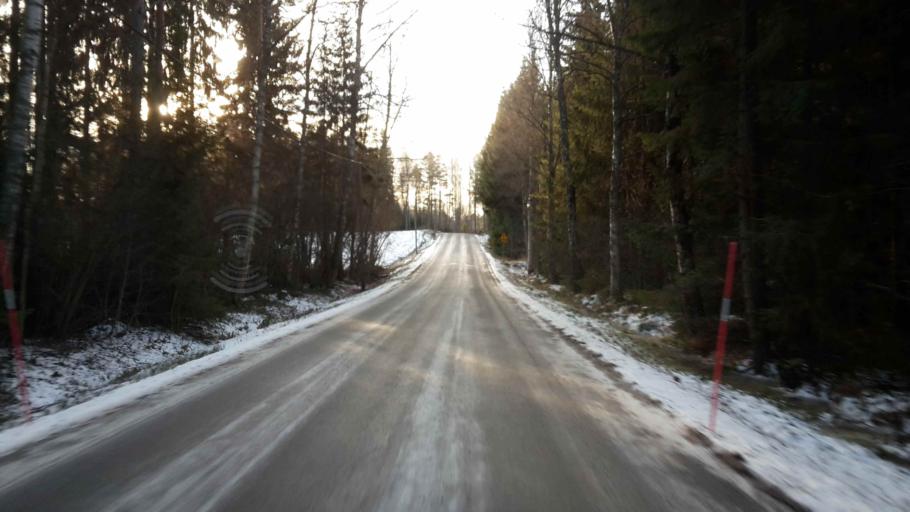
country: SE
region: OEstergoetland
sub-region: Atvidabergs Kommun
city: Atvidaberg
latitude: 58.2660
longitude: 16.1417
